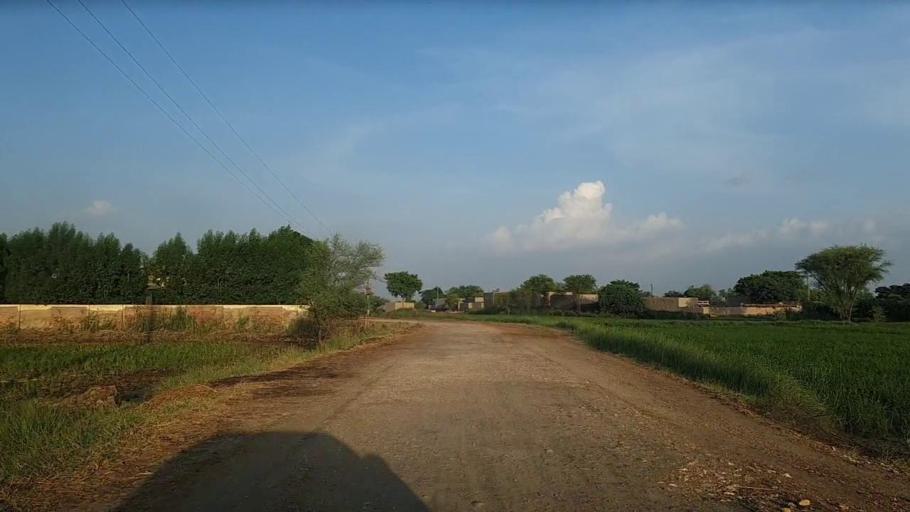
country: PK
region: Sindh
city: Karaundi
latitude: 27.0429
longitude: 68.4099
